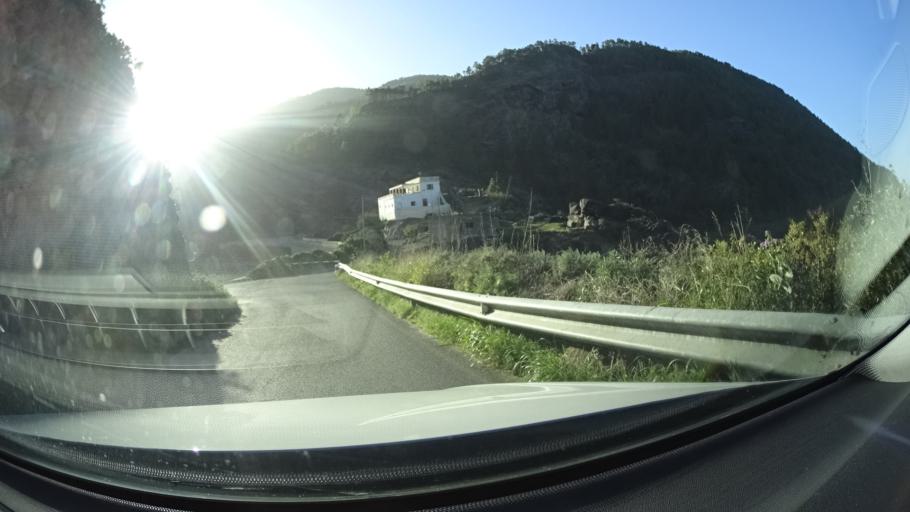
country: ES
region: Canary Islands
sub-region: Provincia de Las Palmas
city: Artenara
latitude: 28.0492
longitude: -15.6675
